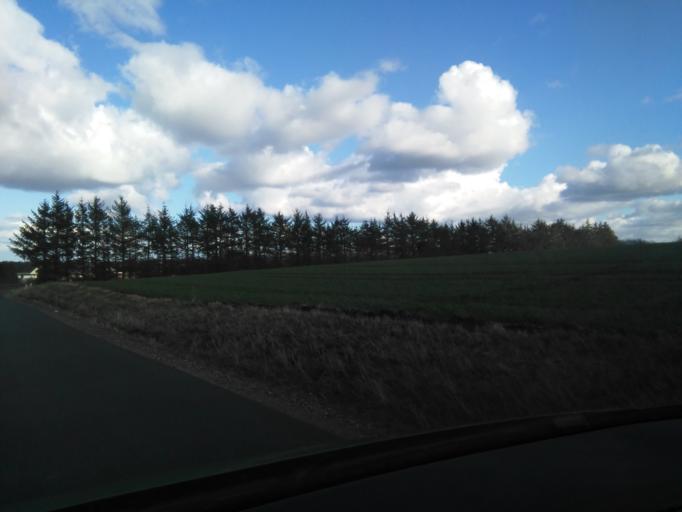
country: DK
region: Central Jutland
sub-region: Silkeborg Kommune
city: Silkeborg
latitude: 56.1914
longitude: 9.4763
